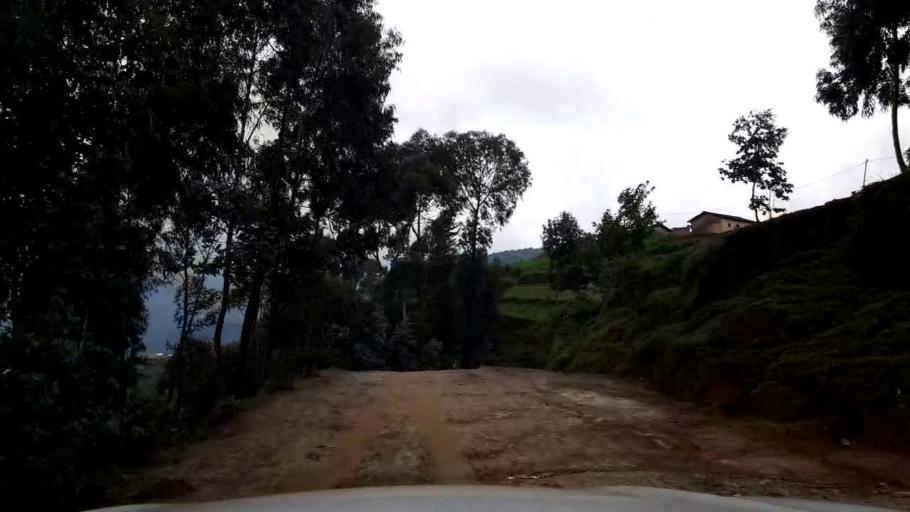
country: RW
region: Western Province
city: Kibuye
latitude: -1.9629
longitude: 29.4782
